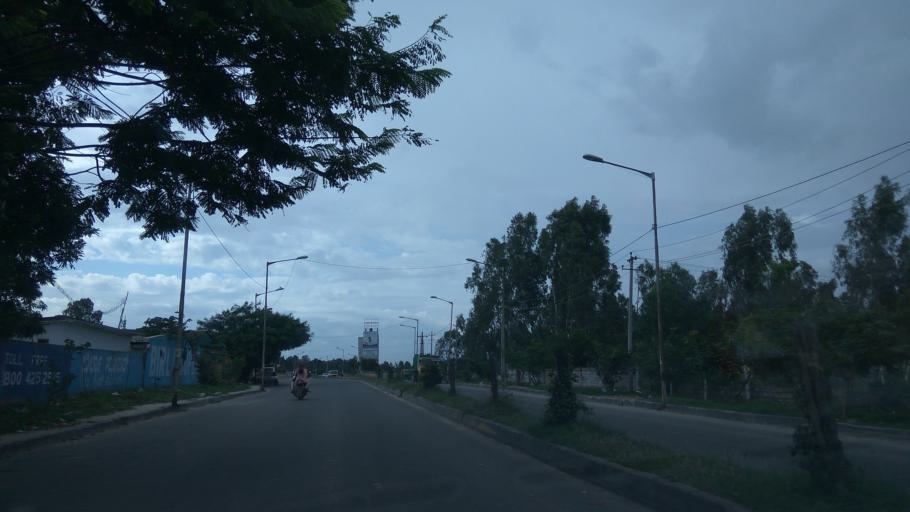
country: IN
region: Karnataka
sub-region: Bangalore Urban
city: Yelahanka
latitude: 13.1002
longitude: 77.6353
